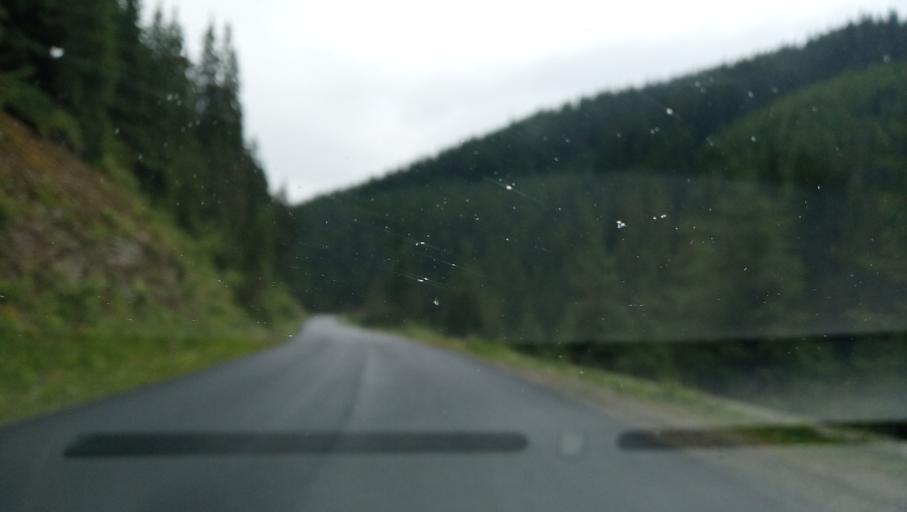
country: RO
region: Hunedoara
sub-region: Oras Petrila
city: Petrila
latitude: 45.4120
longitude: 23.5964
